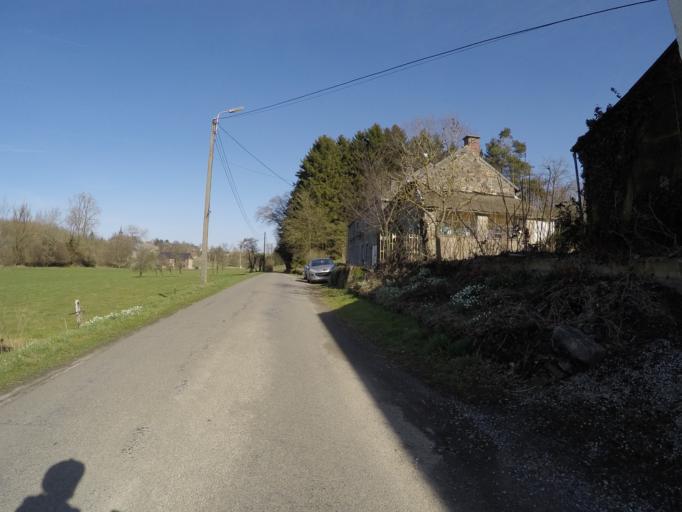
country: BE
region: Wallonia
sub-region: Province de Namur
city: Hamois
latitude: 50.3795
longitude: 5.1461
